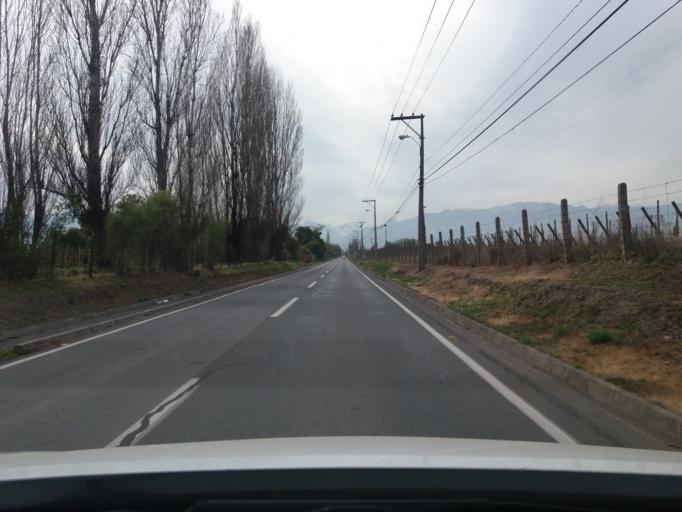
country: CL
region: Valparaiso
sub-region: Provincia de Los Andes
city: Los Andes
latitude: -32.8218
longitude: -70.6718
